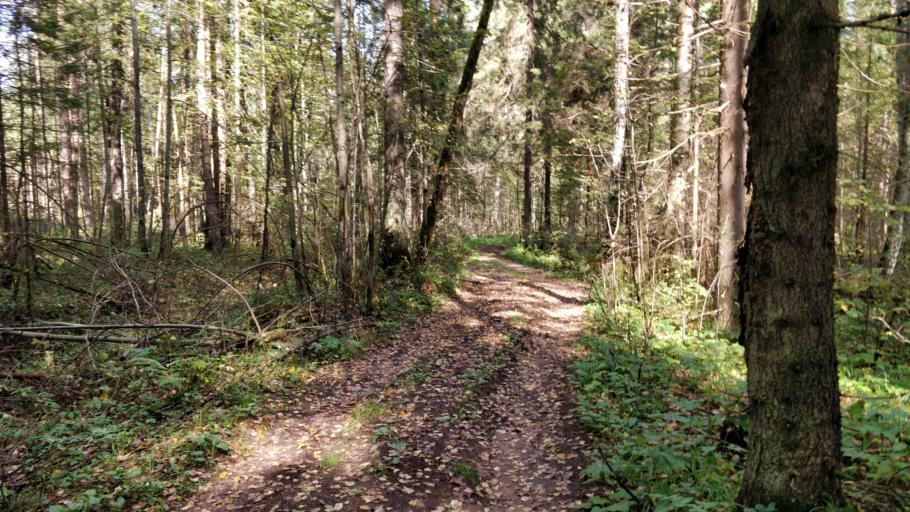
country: RU
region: Perm
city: Perm
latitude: 58.0797
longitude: 56.2129
